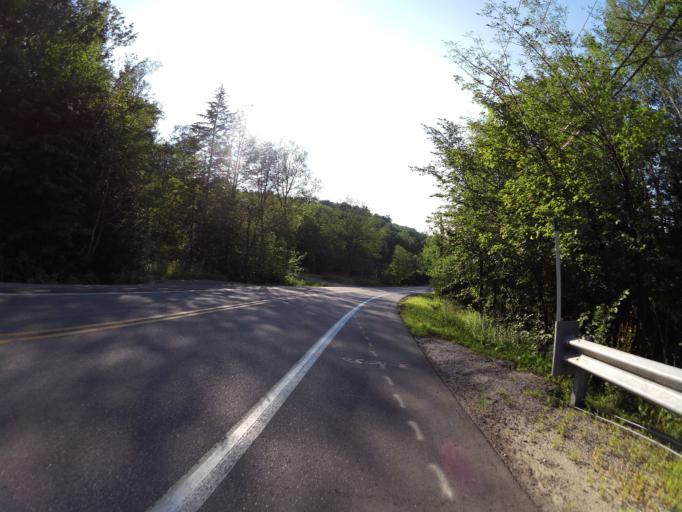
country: CA
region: Quebec
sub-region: Outaouais
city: Wakefield
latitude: 45.5598
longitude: -75.8387
